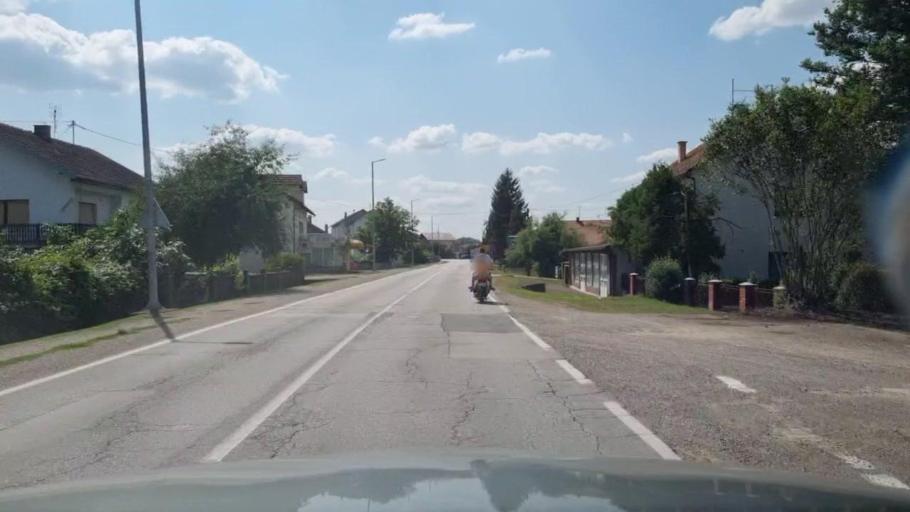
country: HR
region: Vukovarsko-Srijemska
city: Stitar
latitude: 45.0631
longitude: 18.5854
